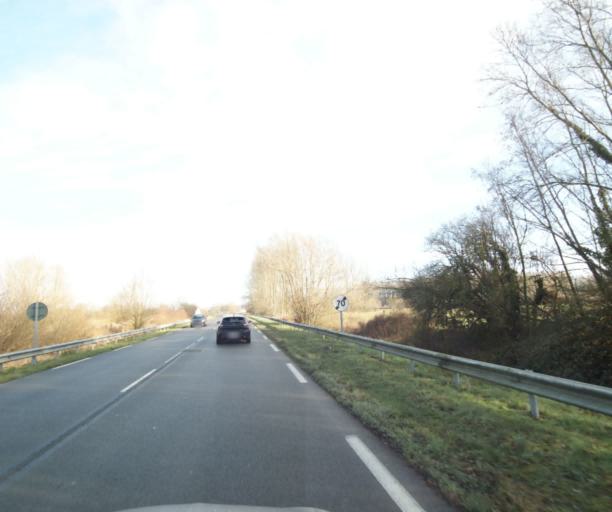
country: FR
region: Nord-Pas-de-Calais
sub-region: Departement du Nord
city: Maing
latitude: 50.3091
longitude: 3.4738
